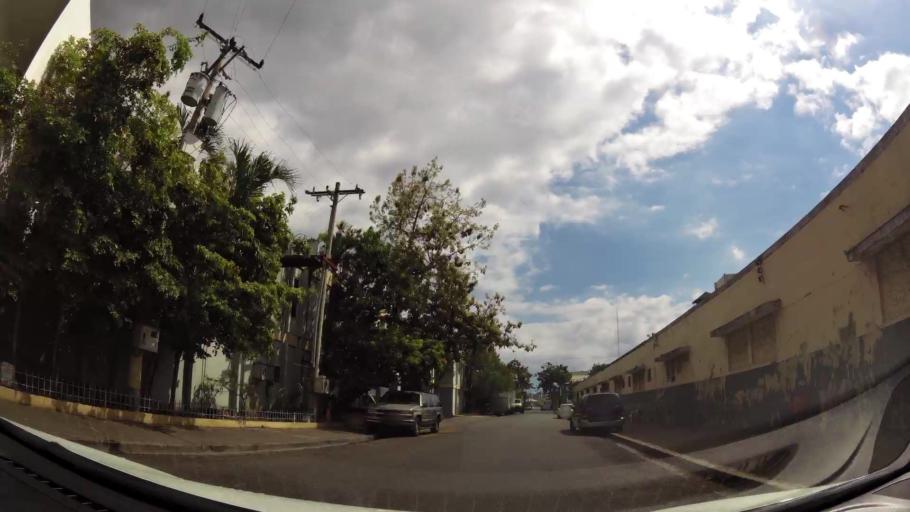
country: DO
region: Nacional
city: La Agustina
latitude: 18.4935
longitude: -69.9227
